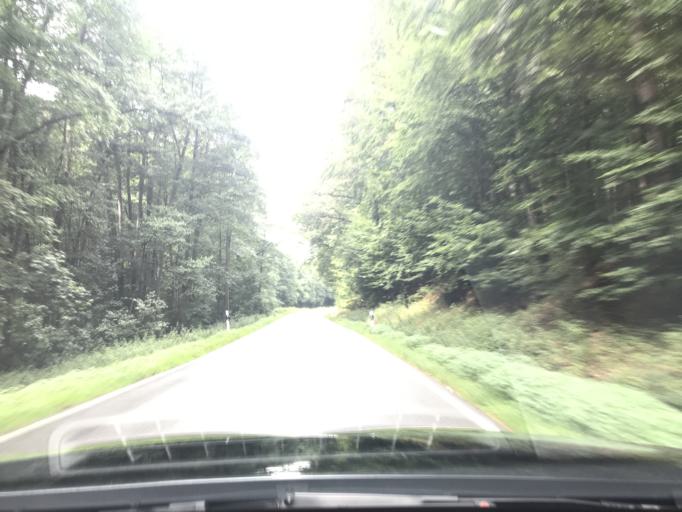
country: DE
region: Bavaria
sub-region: Regierungsbezirk Unterfranken
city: Breitbrunn
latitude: 50.0329
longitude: 10.6738
